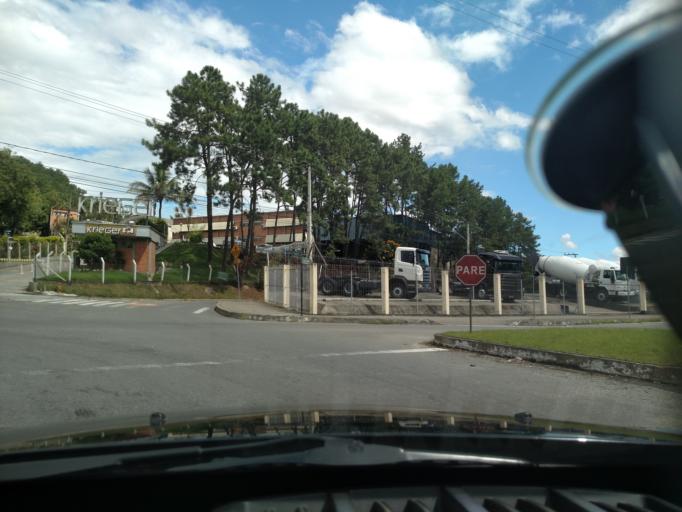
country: BR
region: Santa Catarina
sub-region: Blumenau
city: Blumenau
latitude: -26.8737
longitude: -49.1064
